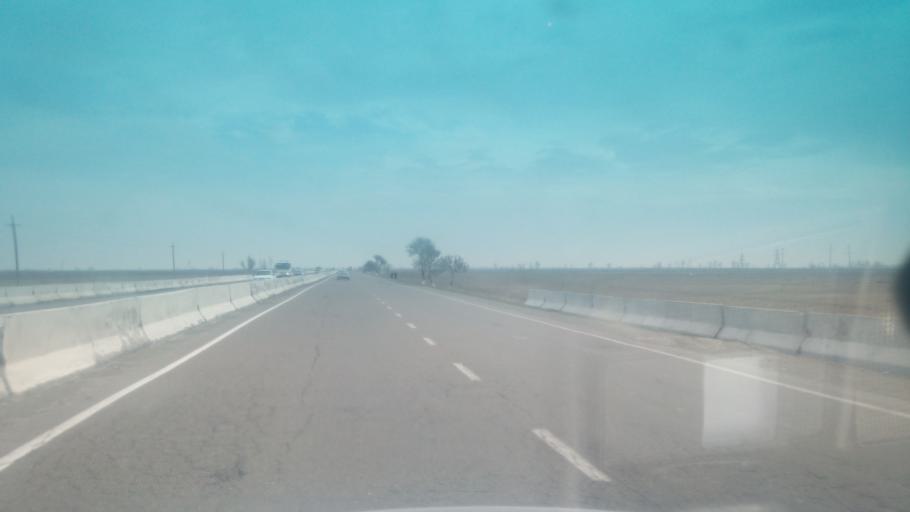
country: KZ
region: Ongtustik Qazaqstan
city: Myrzakent
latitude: 40.5213
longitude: 68.4626
